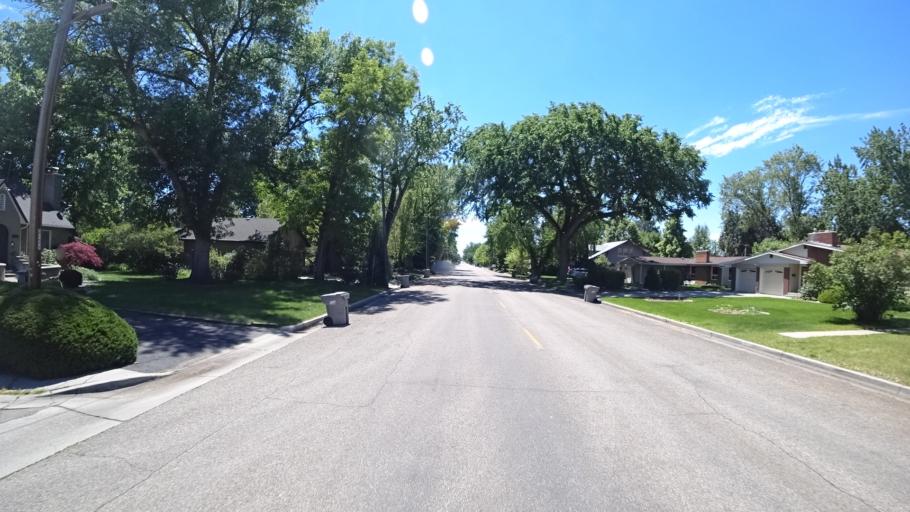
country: US
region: Idaho
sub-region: Ada County
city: Boise
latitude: 43.5991
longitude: -116.2235
